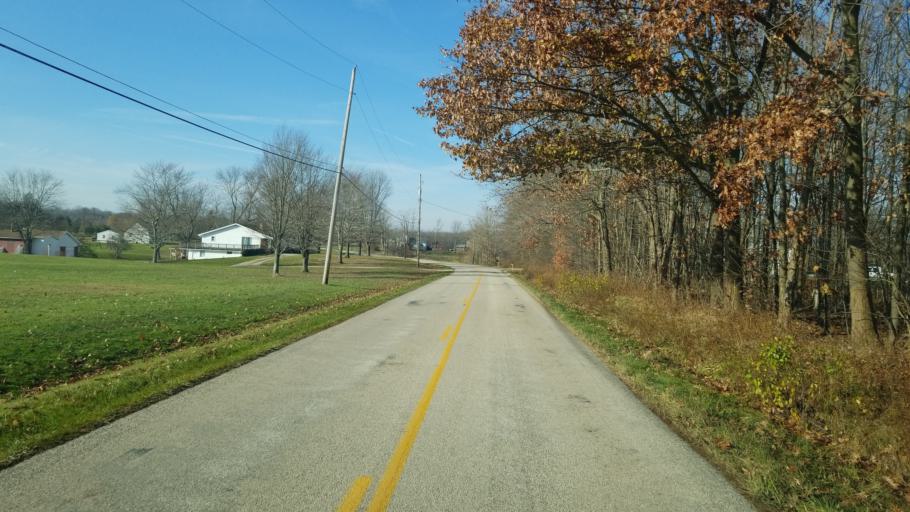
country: US
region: Ohio
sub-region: Ashtabula County
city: North Kingsville
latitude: 41.8246
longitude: -80.6949
